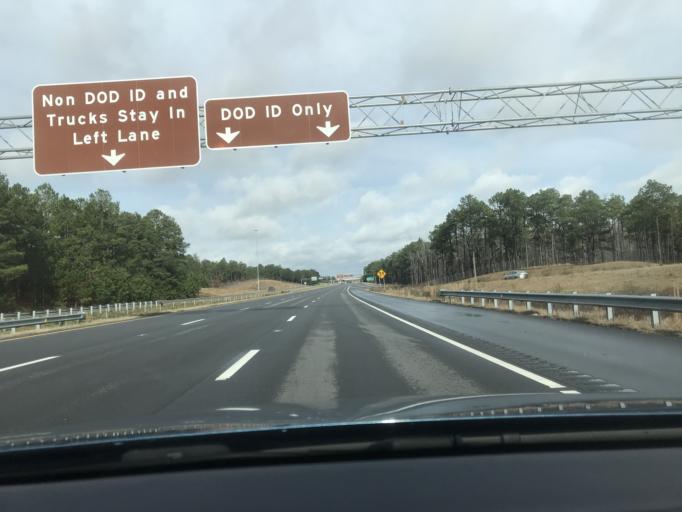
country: US
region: North Carolina
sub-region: Cumberland County
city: Fort Bragg
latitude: 35.1139
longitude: -78.9757
